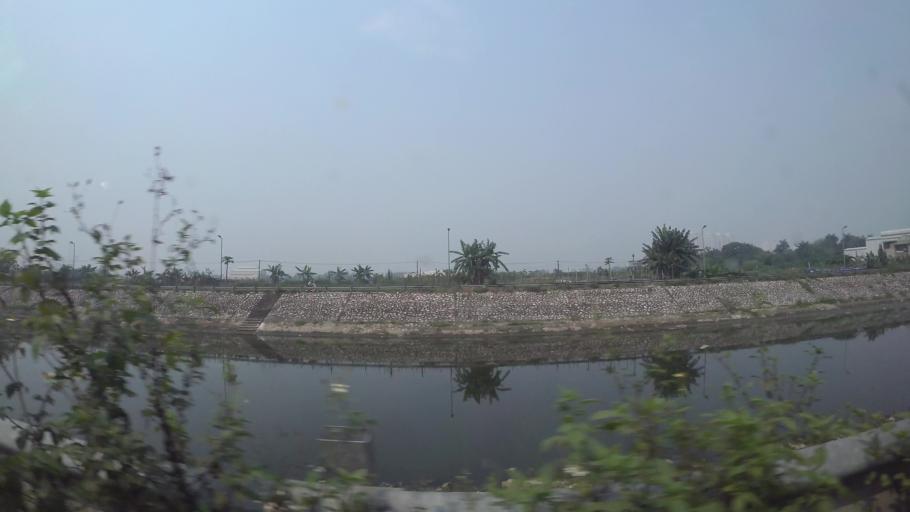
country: VN
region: Ha Noi
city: Van Dien
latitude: 20.9585
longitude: 105.8196
